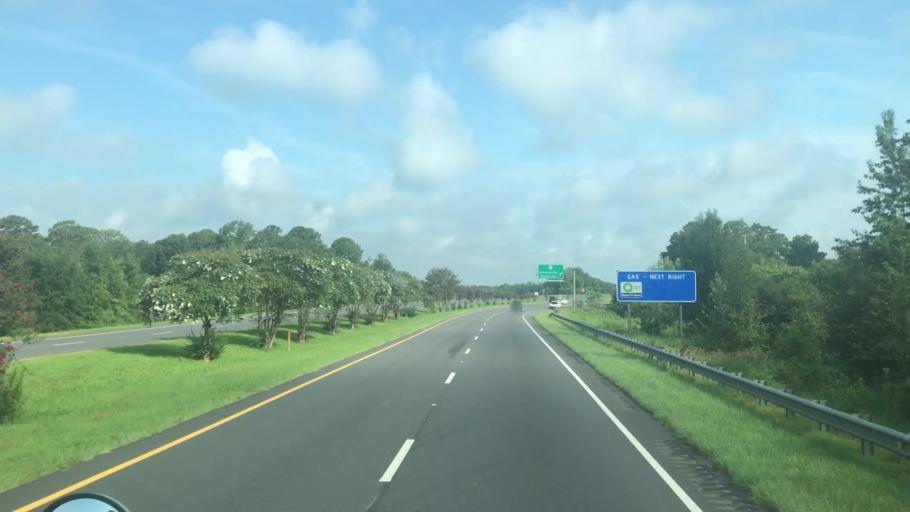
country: US
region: Georgia
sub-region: Decatur County
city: Bainbridge
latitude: 30.9155
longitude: -84.5983
